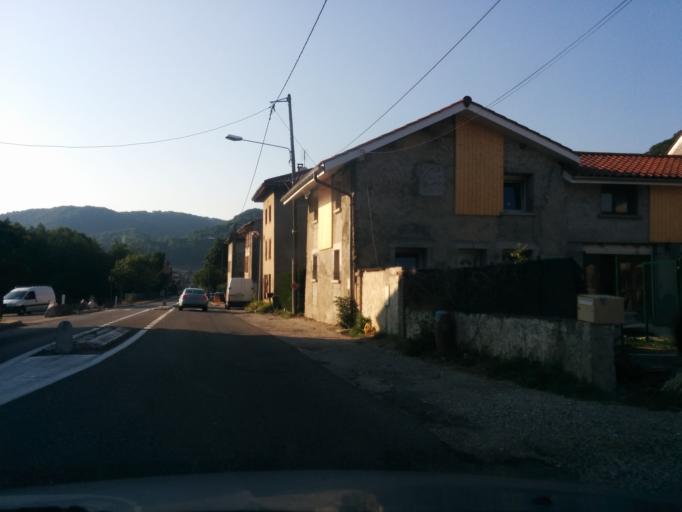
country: FR
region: Rhone-Alpes
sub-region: Departement de l'Isere
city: Chirens
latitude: 45.4083
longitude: 5.5617
